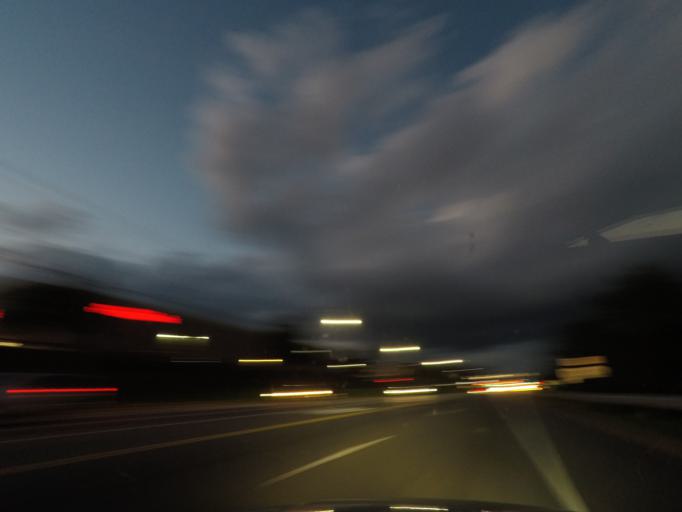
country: US
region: New York
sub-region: Orange County
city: Gardnertown
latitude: 41.5023
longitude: -74.0700
